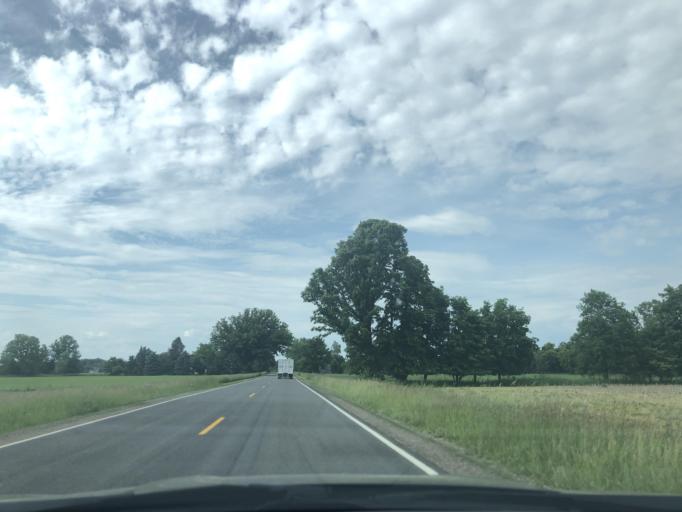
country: US
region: Michigan
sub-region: Clinton County
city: Saint Johns
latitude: 42.9638
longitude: -84.4837
